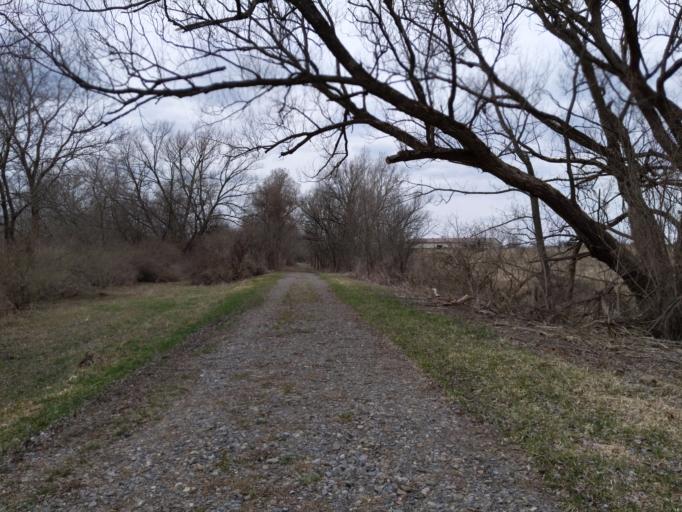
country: US
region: New York
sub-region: Tompkins County
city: Dryden
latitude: 42.5019
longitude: -76.3369
